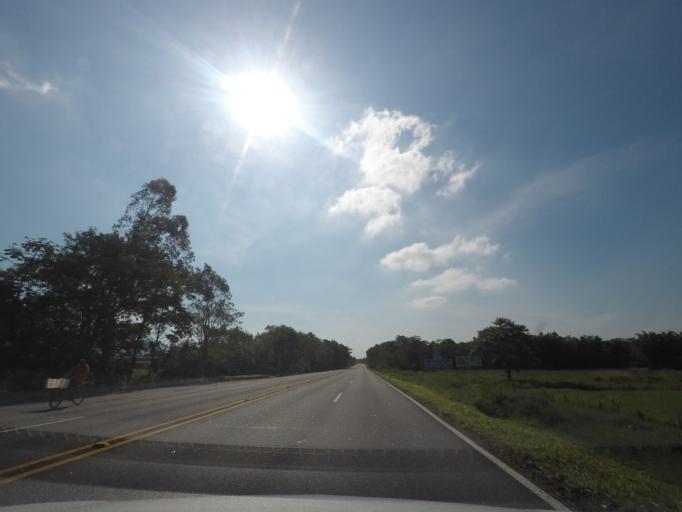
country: BR
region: Parana
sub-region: Pontal Do Parana
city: Pontal do Parana
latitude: -25.6366
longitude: -48.5932
